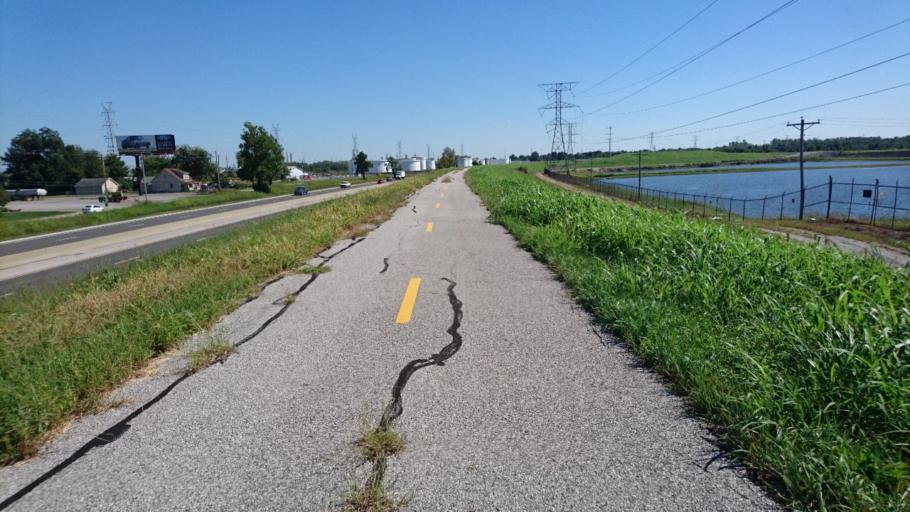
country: US
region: Illinois
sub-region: Madison County
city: Wood River
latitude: 38.8505
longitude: -90.1018
